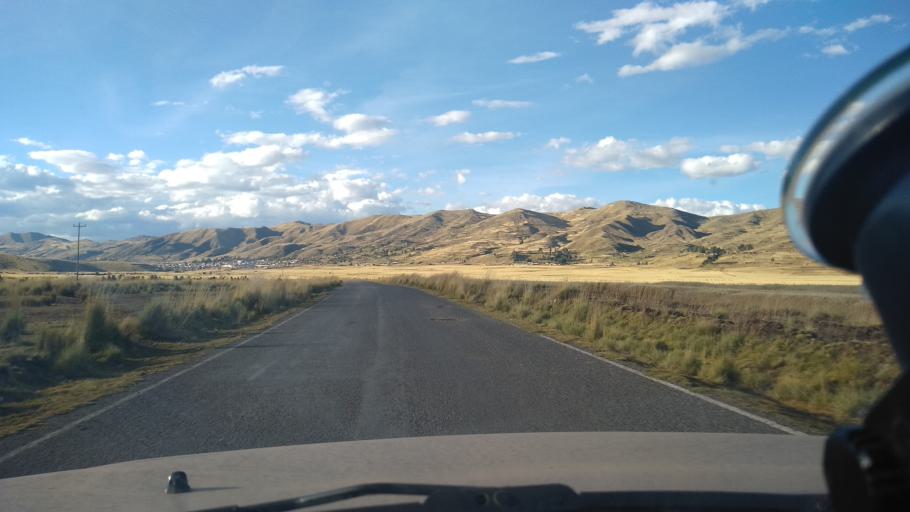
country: PE
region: Cusco
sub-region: Provincia de Canas
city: Chignayhua
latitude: -14.2484
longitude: -71.4351
